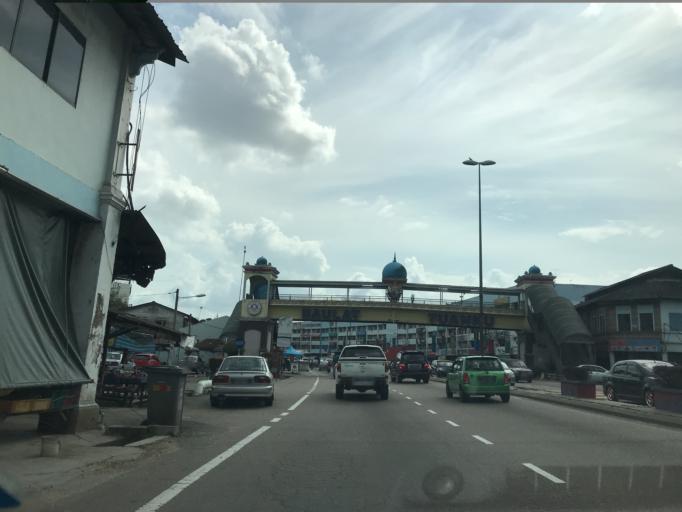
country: MY
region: Johor
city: Taman Senai
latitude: 1.6017
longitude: 103.6452
